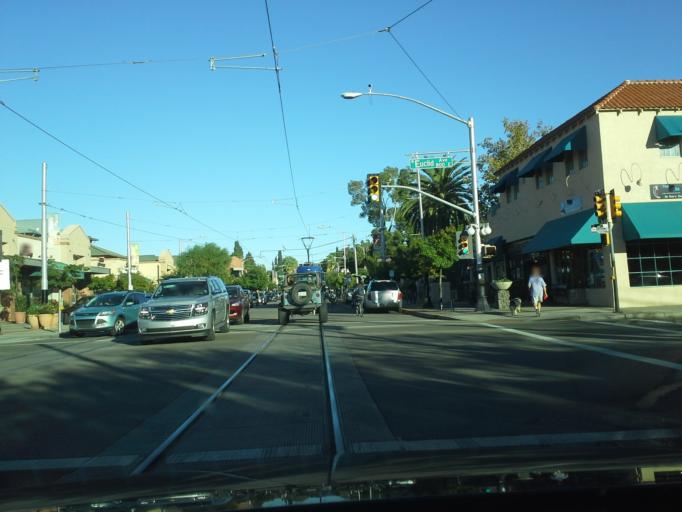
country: US
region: Arizona
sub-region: Pima County
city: South Tucson
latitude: 32.2317
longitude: -110.9596
